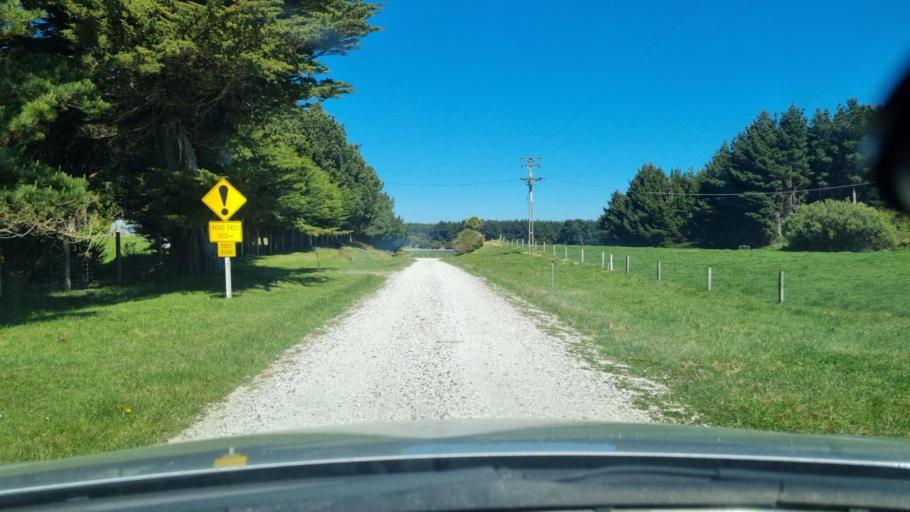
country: NZ
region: Southland
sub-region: Invercargill City
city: Invercargill
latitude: -46.4577
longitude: 168.2713
